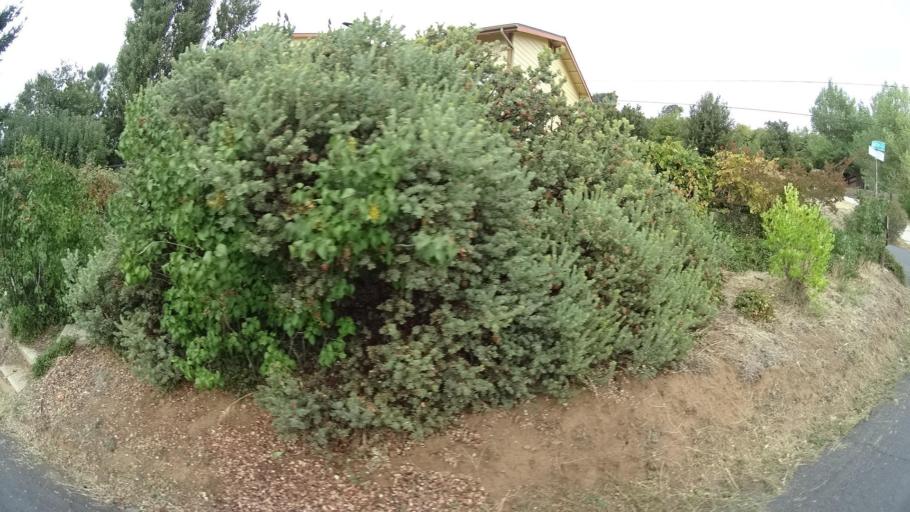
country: US
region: California
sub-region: San Diego County
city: Julian
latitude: 32.9958
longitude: -116.5801
